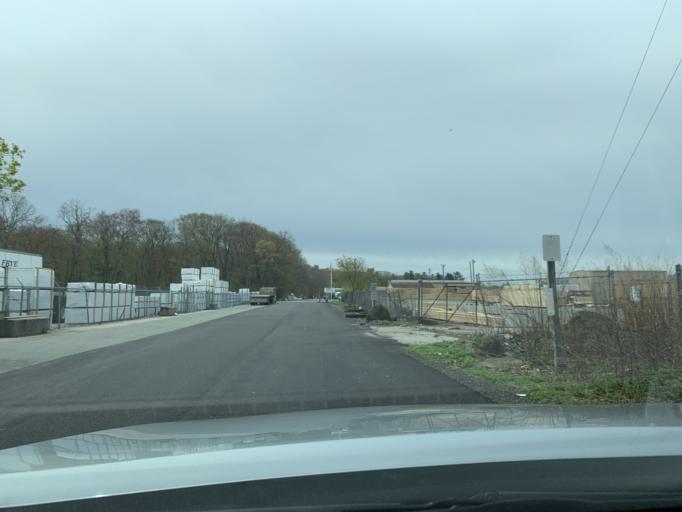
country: US
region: Rhode Island
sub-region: Washington County
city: North Kingstown
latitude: 41.6054
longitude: -71.4683
